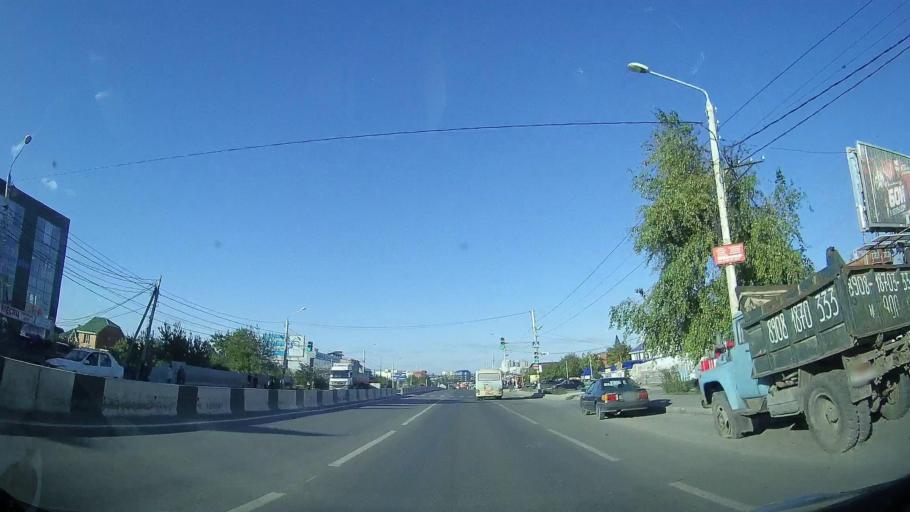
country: RU
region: Rostov
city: Kalinin
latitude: 47.2163
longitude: 39.6135
